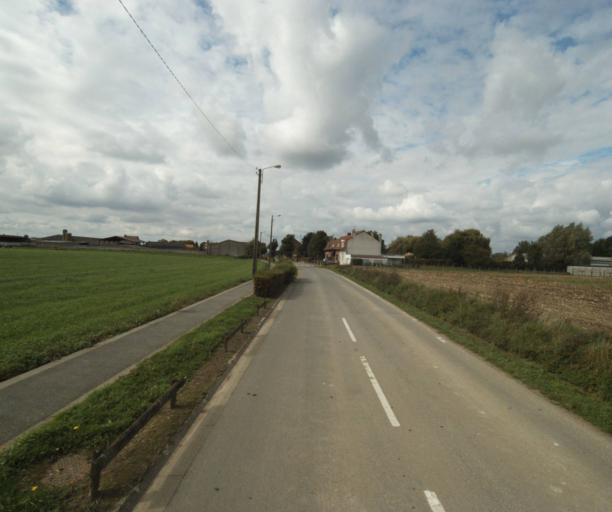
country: FR
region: Nord-Pas-de-Calais
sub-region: Departement du Nord
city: Premesques
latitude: 50.6628
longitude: 2.9400
